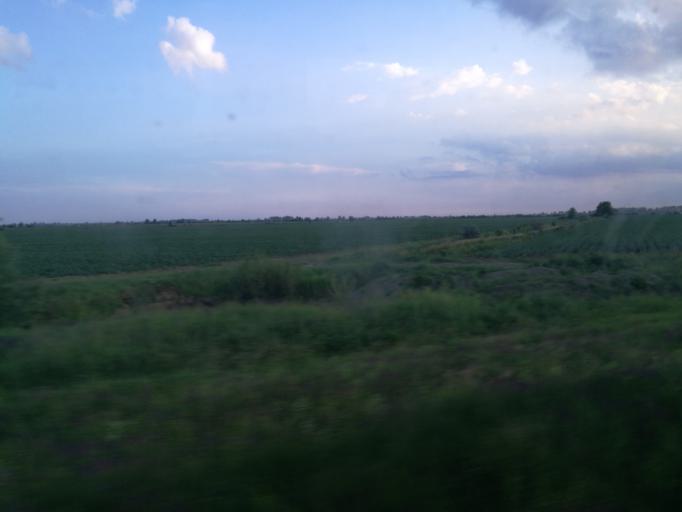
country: RO
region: Dambovita
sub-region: Comuna Contesti
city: Balteni
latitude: 44.6506
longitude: 25.6830
